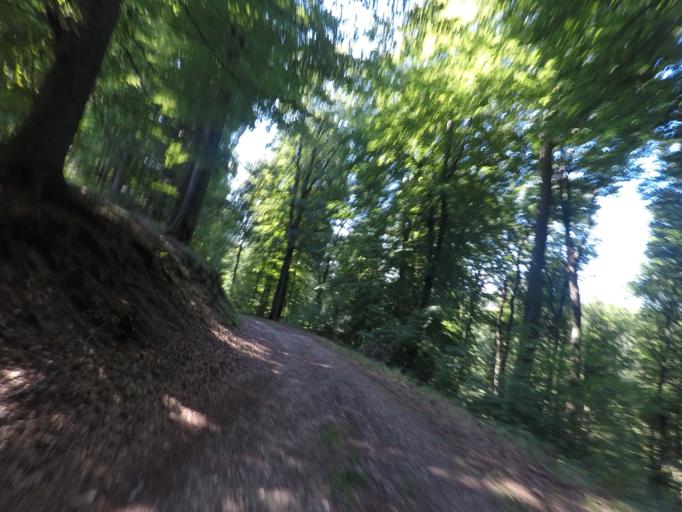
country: LU
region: Luxembourg
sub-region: Canton de Capellen
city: Kopstal
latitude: 49.6563
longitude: 6.0704
